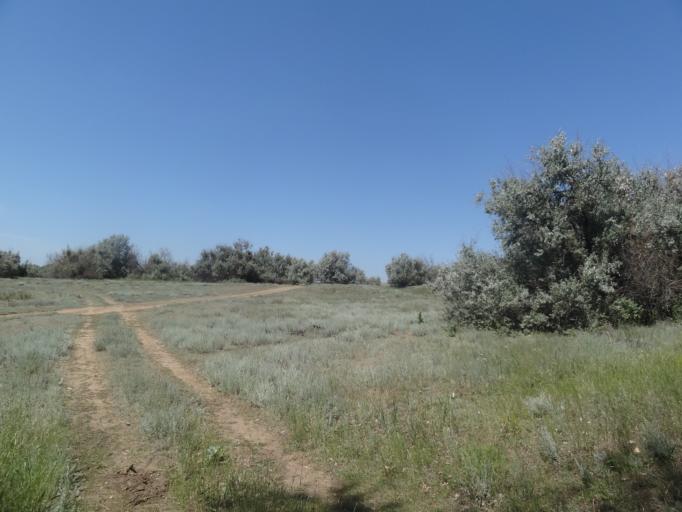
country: RU
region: Saratov
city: Krasnoarmeysk
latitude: 51.1489
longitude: 45.9327
